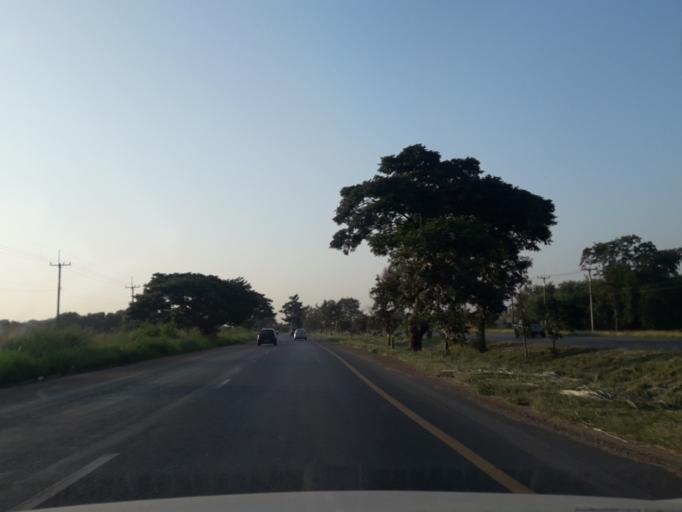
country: TH
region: Phra Nakhon Si Ayutthaya
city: Bang Pa-in
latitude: 14.2248
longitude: 100.5408
